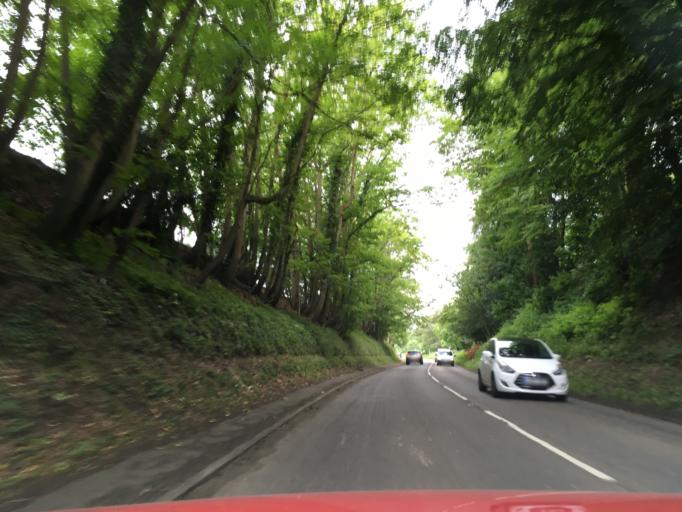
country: GB
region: England
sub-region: Central Bedfordshire
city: Aspley Guise
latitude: 51.9968
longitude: -0.6338
